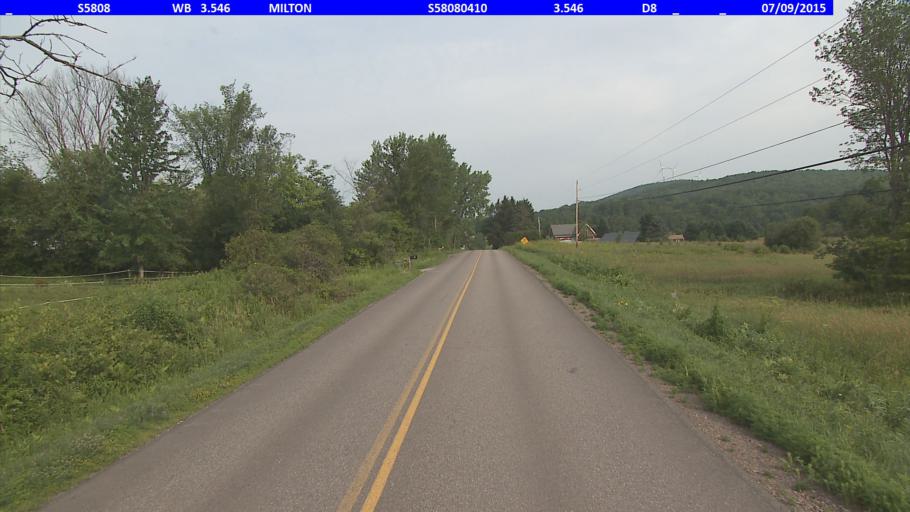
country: US
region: Vermont
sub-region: Chittenden County
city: Milton
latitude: 44.6369
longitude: -73.0513
